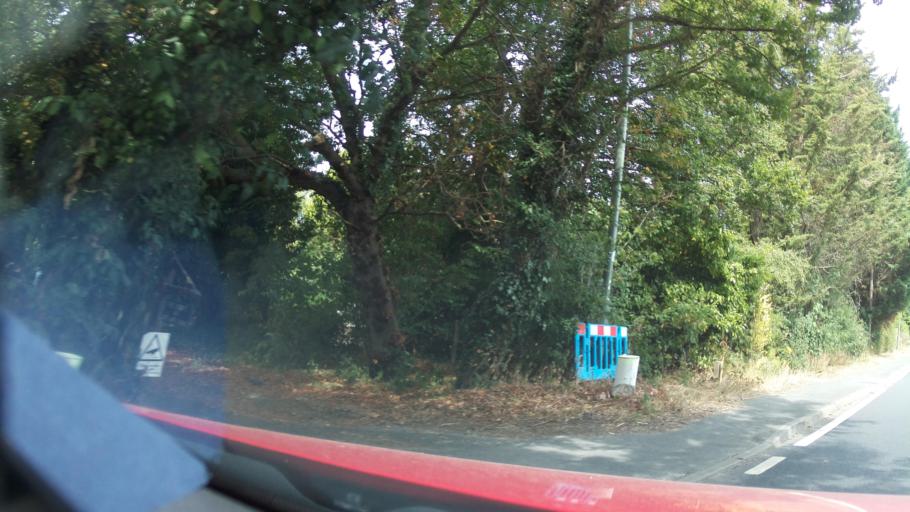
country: GB
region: England
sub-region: Surrey
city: Salfords
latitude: 51.1817
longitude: -0.1954
